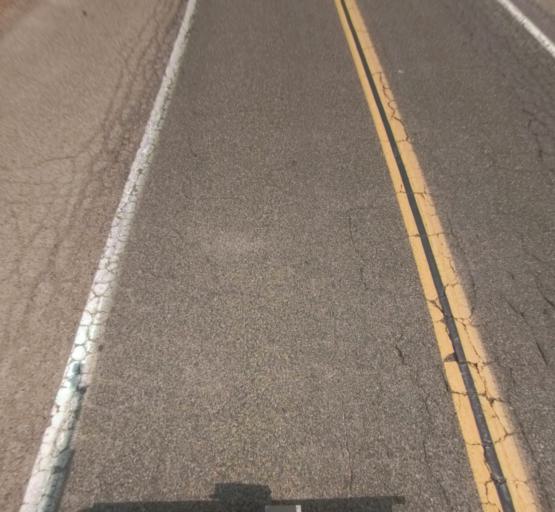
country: US
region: California
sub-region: Madera County
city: Yosemite Lakes
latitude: 37.1922
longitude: -119.9091
